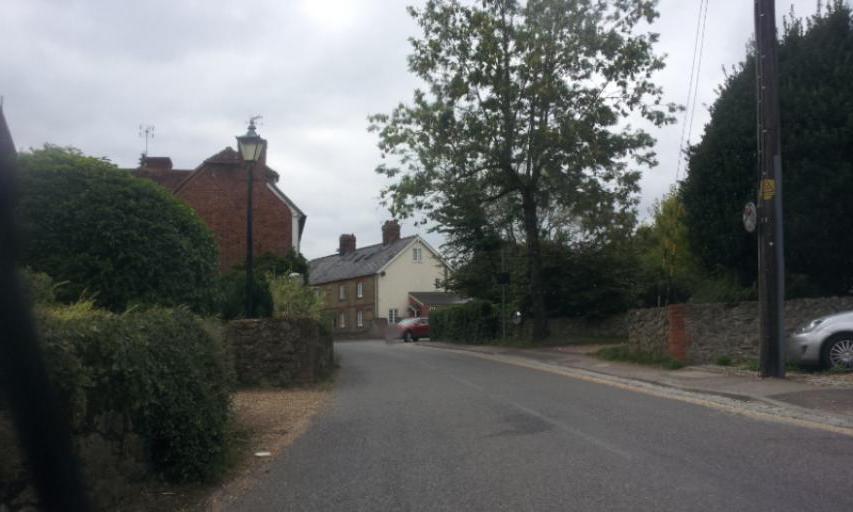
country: GB
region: England
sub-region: Kent
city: Kings Hill
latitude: 51.2905
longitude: 0.3795
